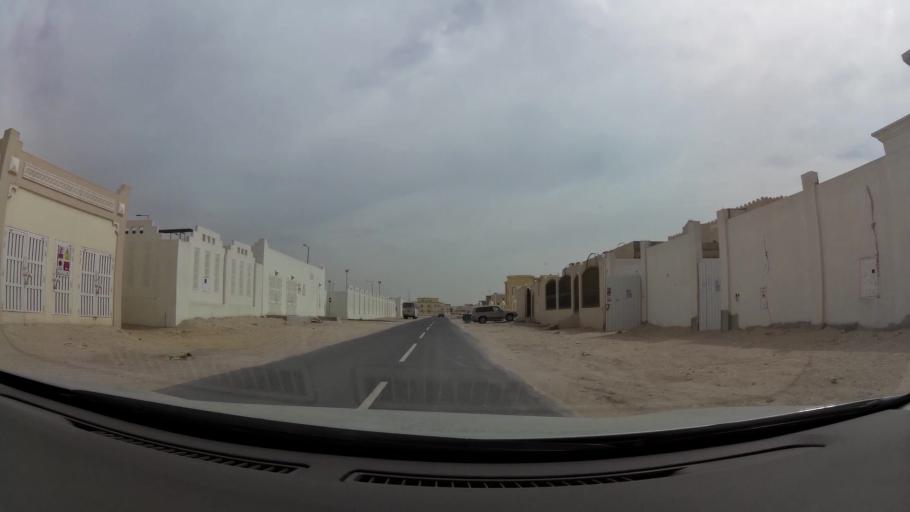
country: QA
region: Baladiyat ad Dawhah
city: Doha
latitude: 25.2119
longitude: 51.4677
